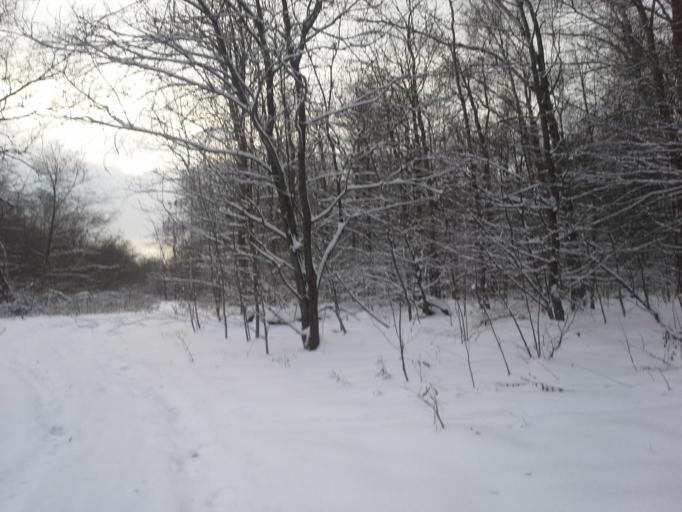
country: RU
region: Moscow
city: Yasenevo
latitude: 55.5903
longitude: 37.5058
